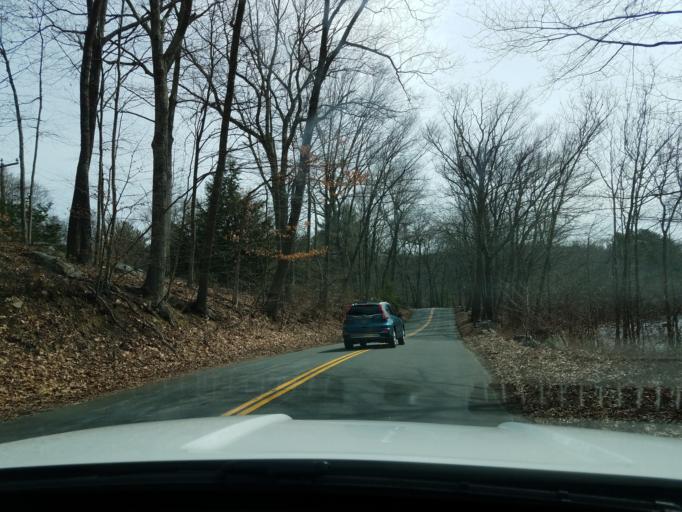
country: US
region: Connecticut
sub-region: Hartford County
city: Collinsville
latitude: 41.7768
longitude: -72.9055
